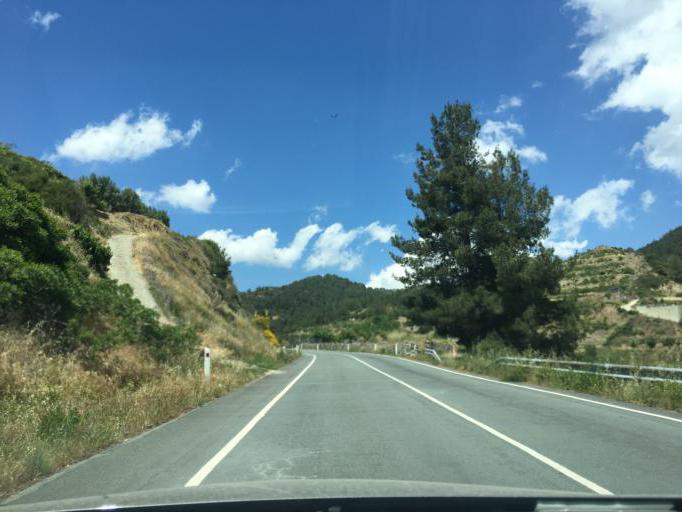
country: CY
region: Limassol
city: Pelendri
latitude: 34.9048
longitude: 32.9427
